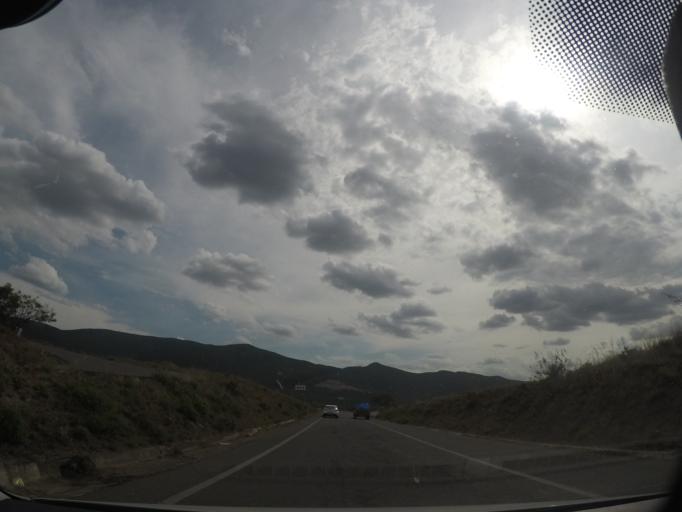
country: MX
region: Oaxaca
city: Santa Maria del Tule
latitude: 17.0366
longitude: -96.6174
